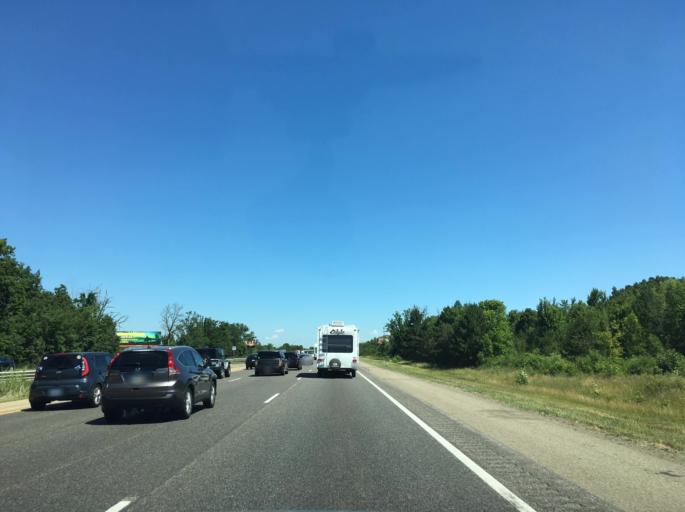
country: US
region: Michigan
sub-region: Genesee County
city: Beecher
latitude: 43.0823
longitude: -83.7627
